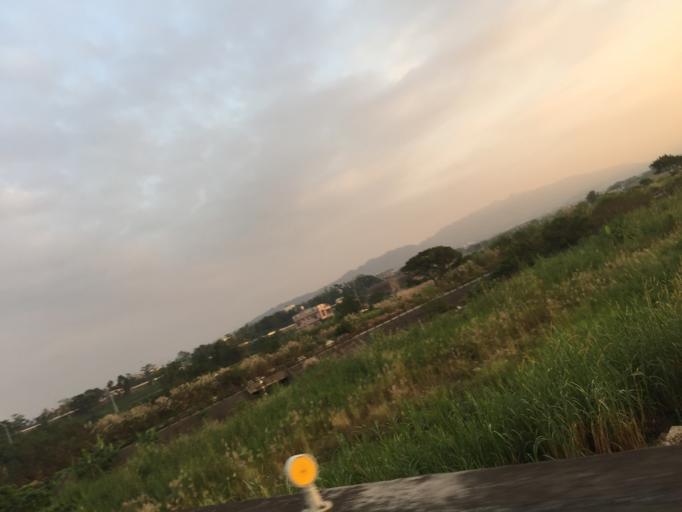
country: TW
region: Taiwan
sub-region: Miaoli
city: Miaoli
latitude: 24.4944
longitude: 120.7800
